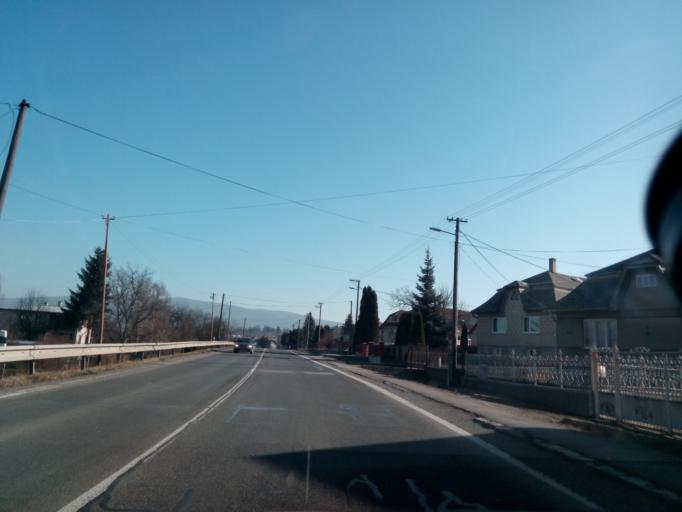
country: SK
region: Kosicky
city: Secovce
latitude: 48.7316
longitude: 21.4623
